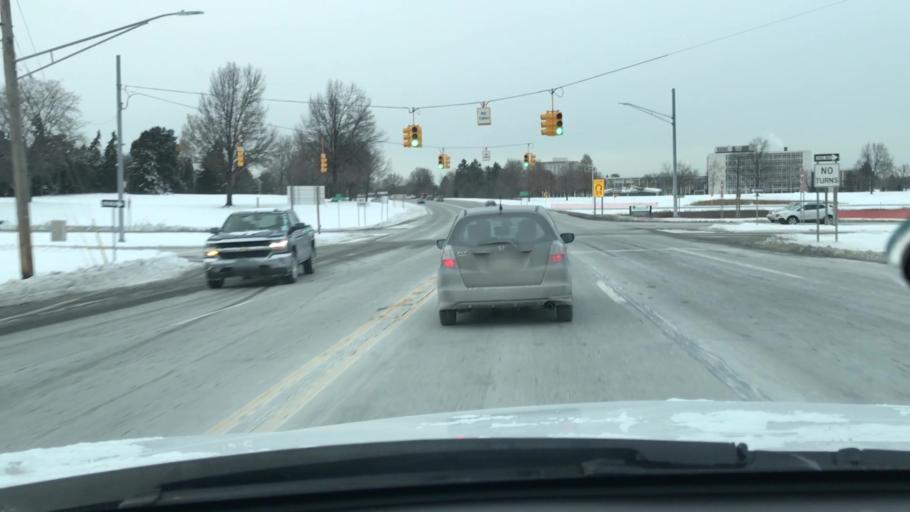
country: US
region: Michigan
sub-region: Oakland County
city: Pontiac
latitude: 42.6502
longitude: -83.3266
